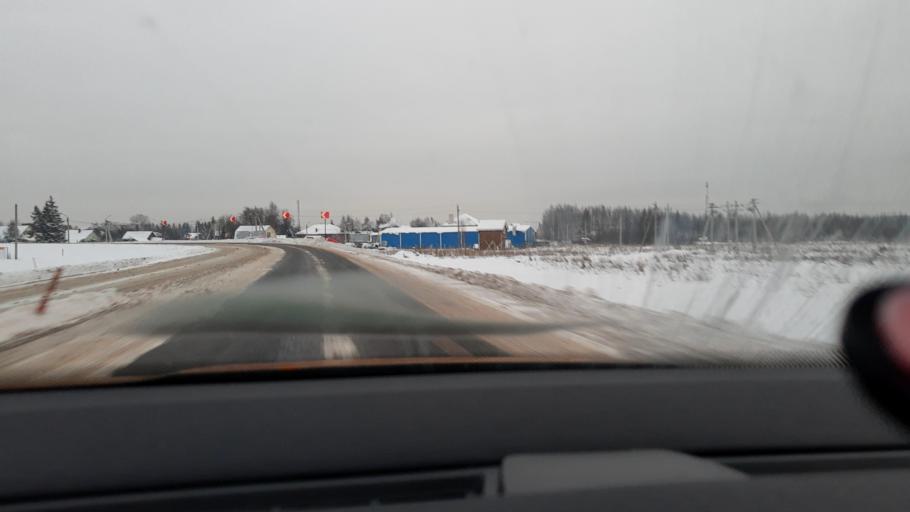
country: RU
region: Moskovskaya
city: Radumlya
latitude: 56.0572
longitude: 37.1439
